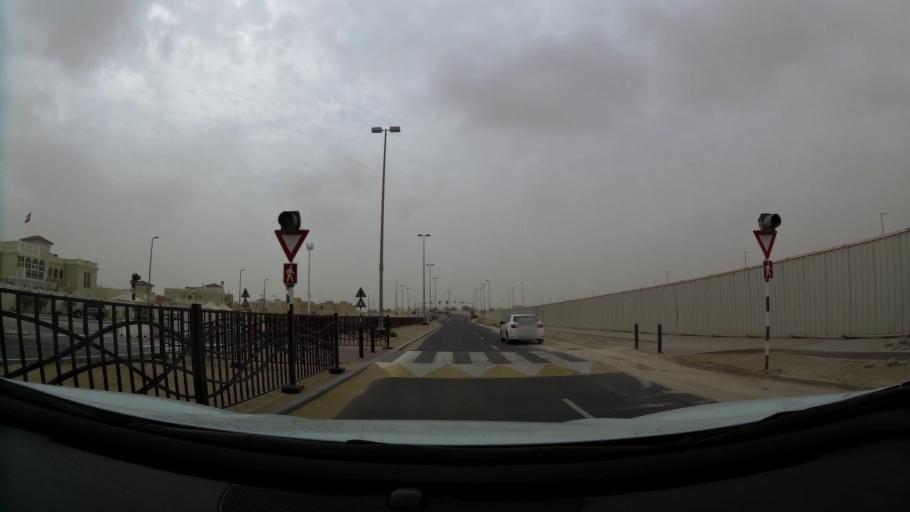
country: AE
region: Abu Dhabi
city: Abu Dhabi
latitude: 24.4318
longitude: 54.7264
